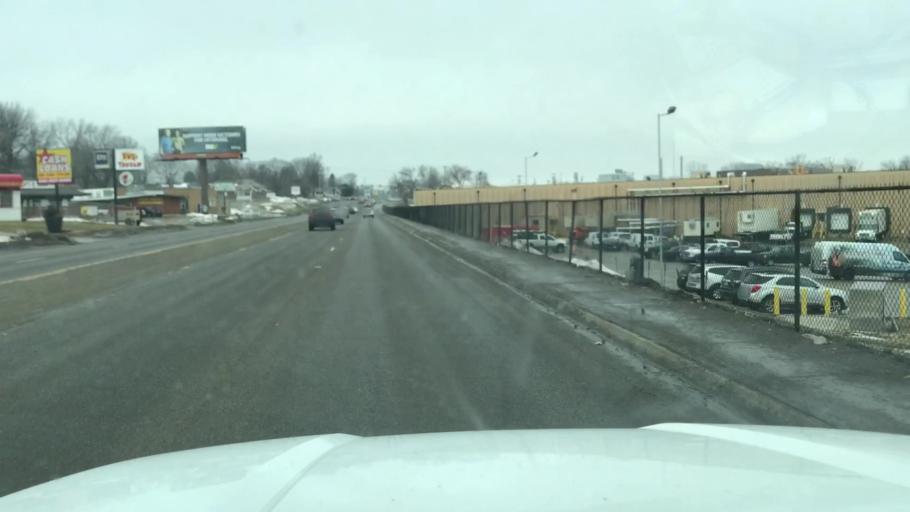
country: US
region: Missouri
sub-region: Buchanan County
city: Saint Joseph
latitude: 39.7895
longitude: -94.8077
